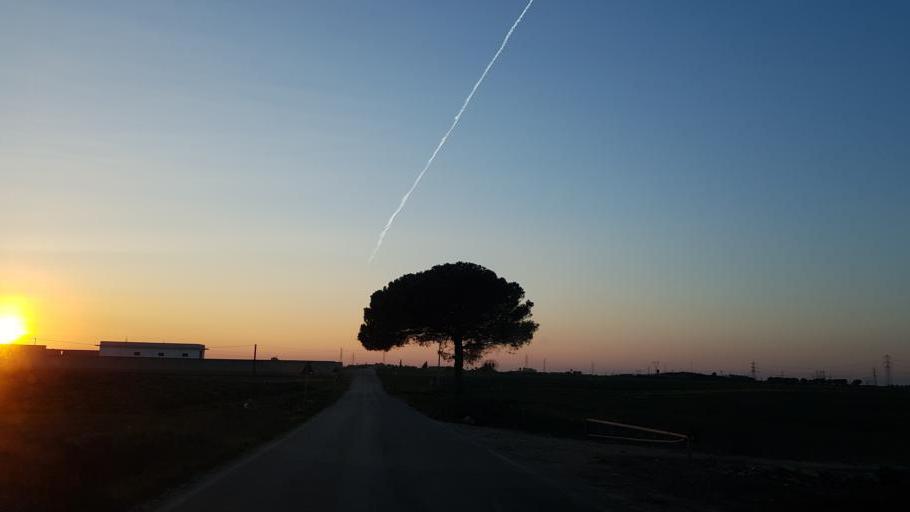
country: IT
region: Apulia
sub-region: Provincia di Brindisi
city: La Rosa
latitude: 40.5902
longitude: 17.9246
